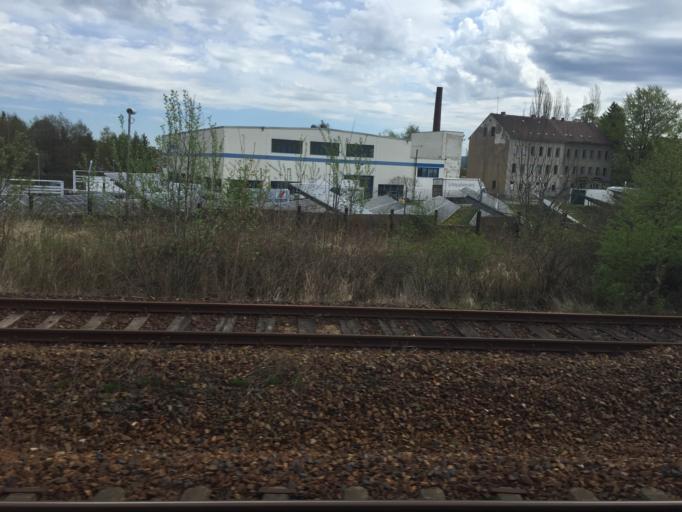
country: DE
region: Saxony
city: Lobau
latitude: 51.1031
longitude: 14.6622
